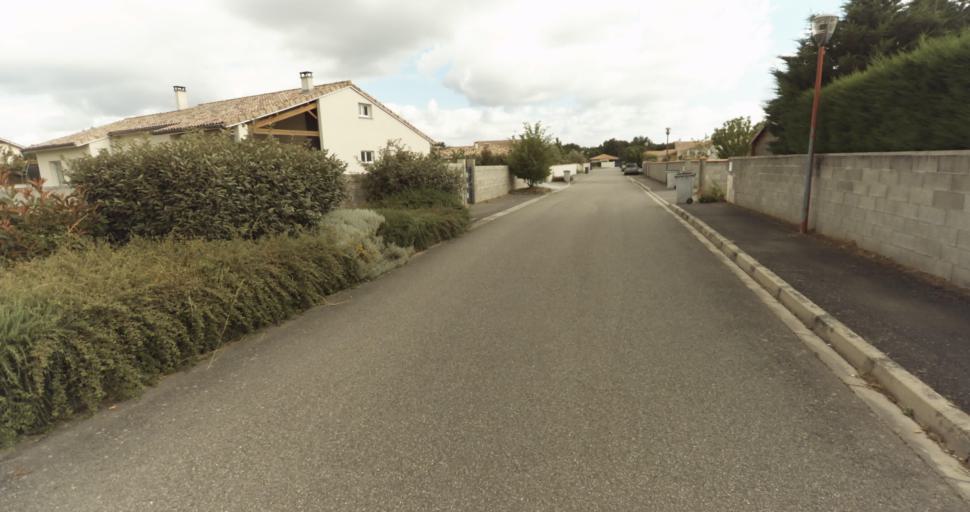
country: FR
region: Midi-Pyrenees
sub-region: Departement de la Haute-Garonne
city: Fonsorbes
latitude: 43.5522
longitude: 1.2302
